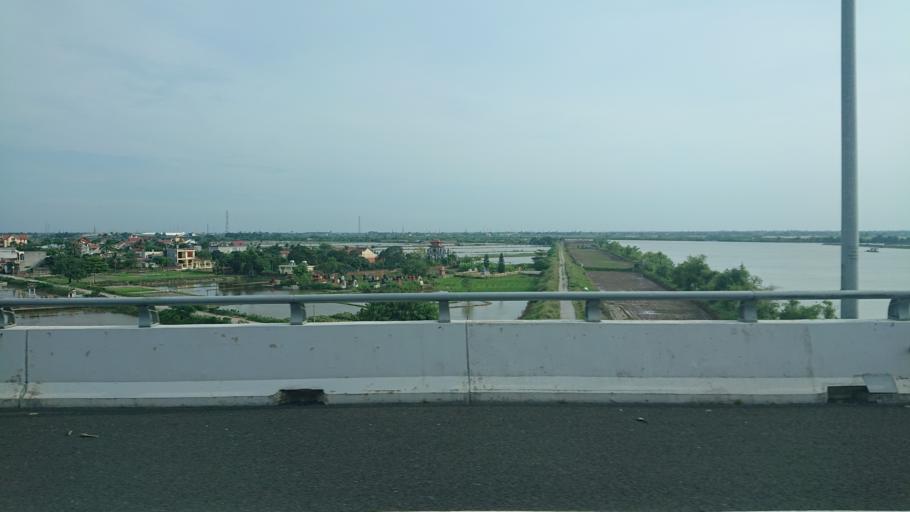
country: VN
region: Hai Phong
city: An Lao
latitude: 20.8072
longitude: 106.5145
